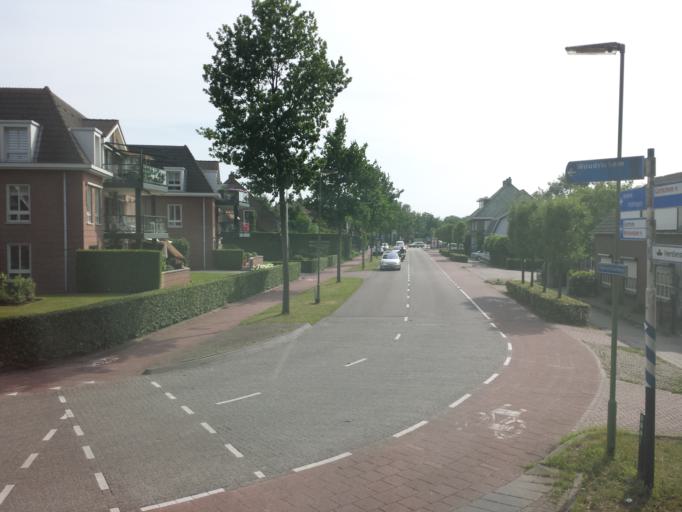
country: NL
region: South Holland
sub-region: Gemeente Gorinchem
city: Gorinchem
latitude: 51.8131
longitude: 4.9569
